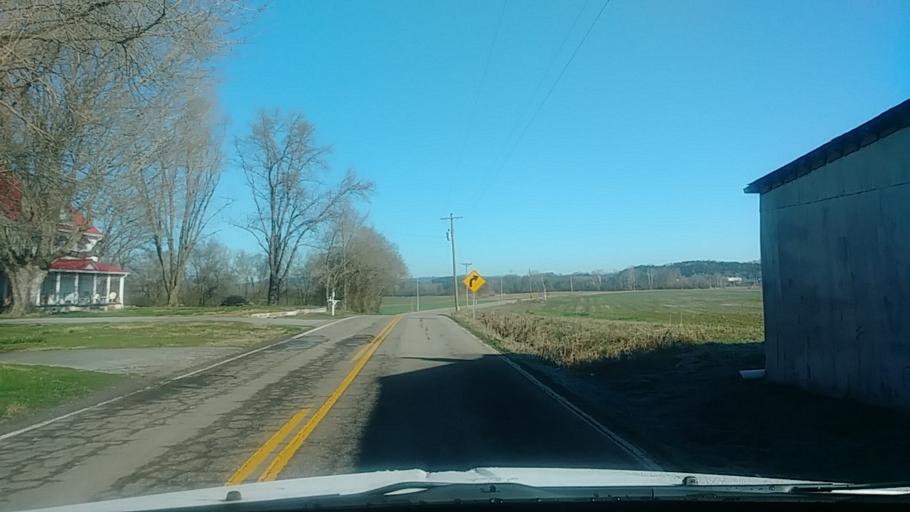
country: US
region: Tennessee
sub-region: Jefferson County
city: White Pine
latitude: 36.1624
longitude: -83.1627
